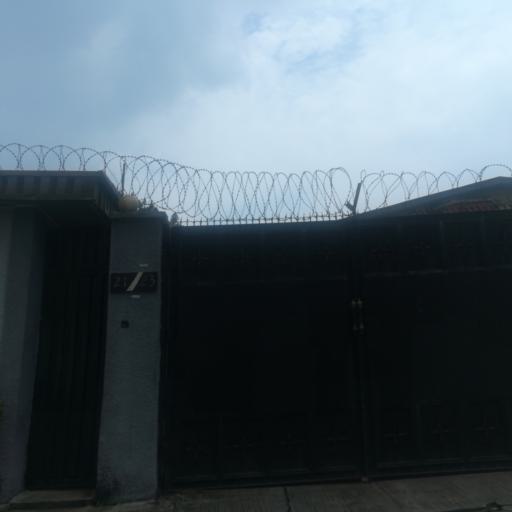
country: NG
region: Lagos
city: Ojota
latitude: 6.5725
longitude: 3.3914
